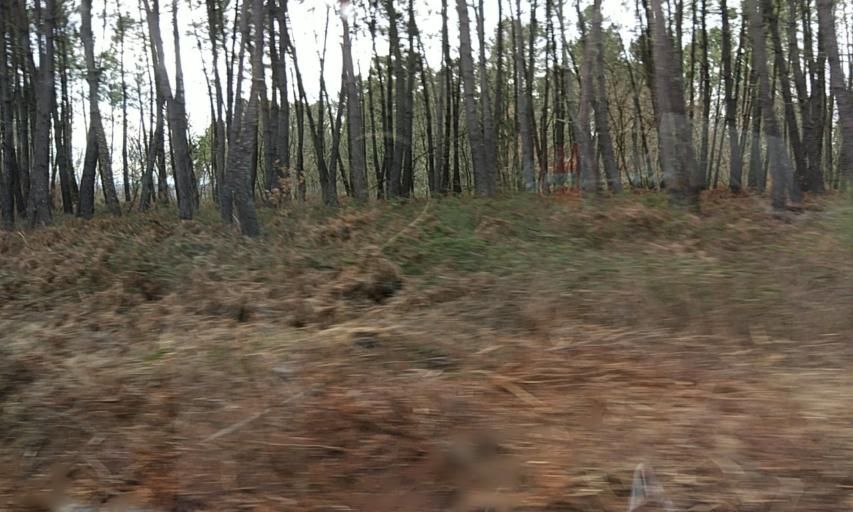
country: ES
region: Castille and Leon
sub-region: Provincia de Salamanca
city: Penaparda
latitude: 40.3001
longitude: -6.6567
